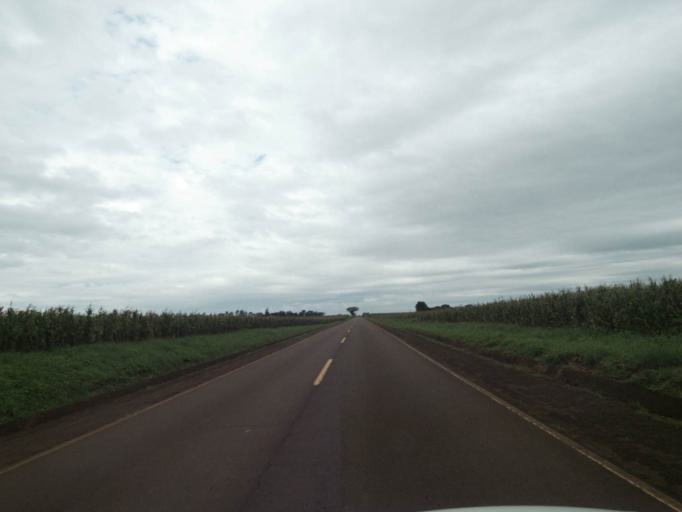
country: BR
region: Parana
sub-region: Marechal Candido Rondon
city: Marechal Candido Rondon
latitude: -24.8139
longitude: -54.1914
